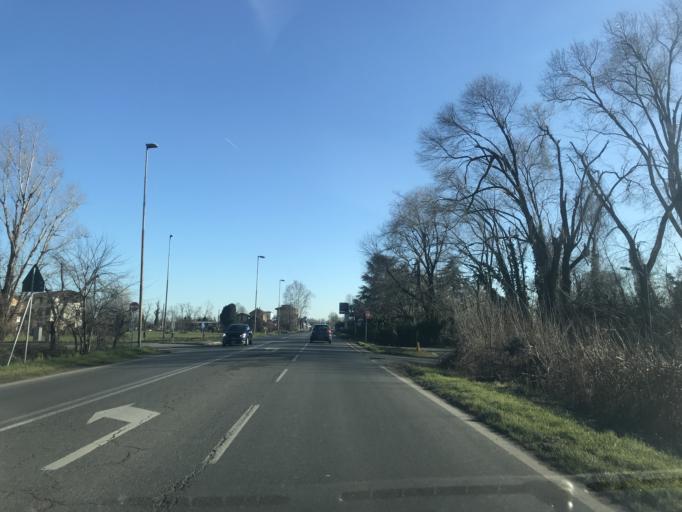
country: IT
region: Lombardy
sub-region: Provincia di Lodi
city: San Martino in Strada
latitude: 45.2913
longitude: 9.5275
